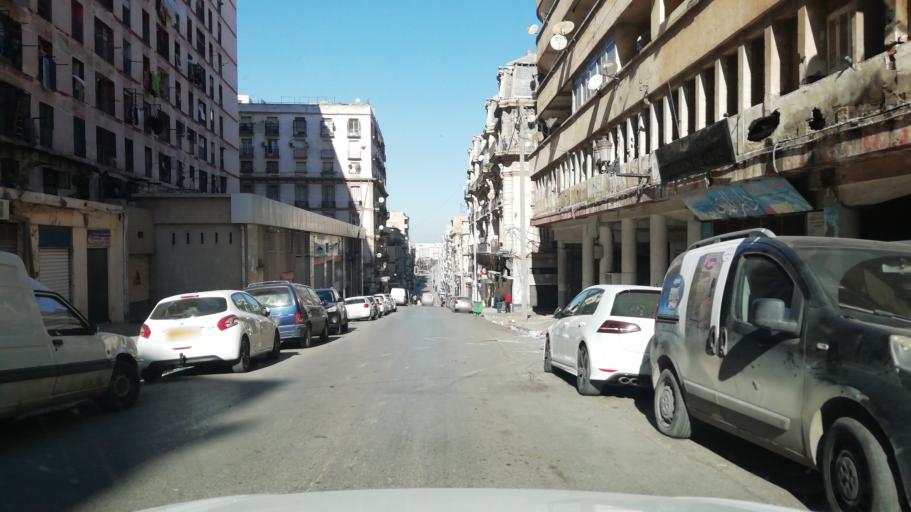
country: DZ
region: Oran
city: Oran
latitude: 35.6989
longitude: -0.6439
